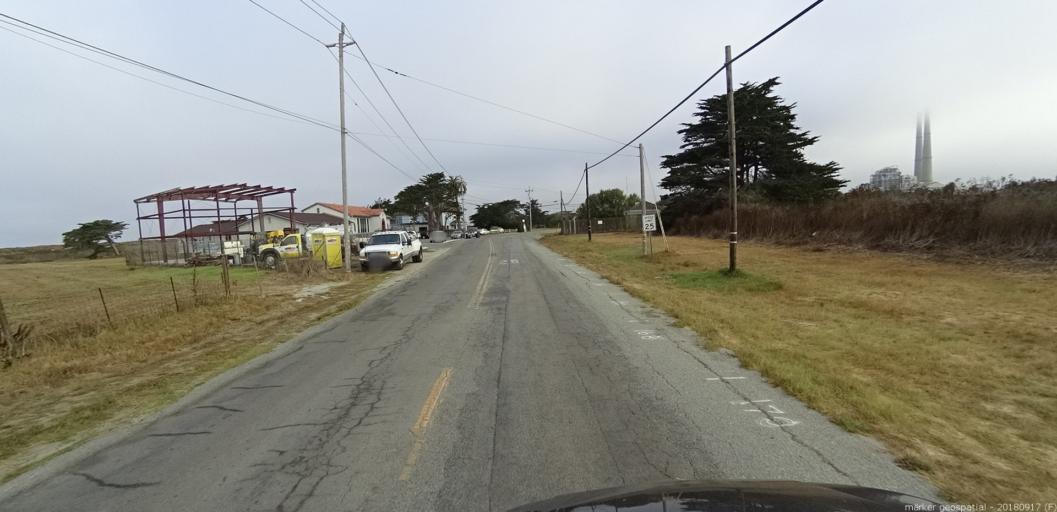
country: US
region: California
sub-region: Monterey County
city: Castroville
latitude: 36.7961
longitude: -121.7857
